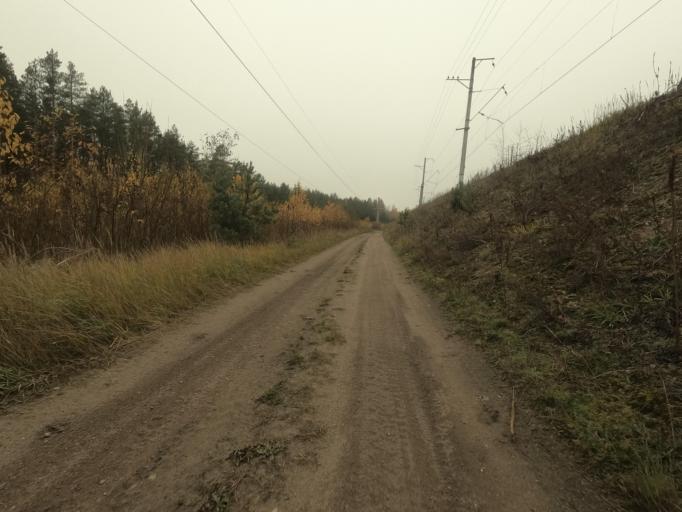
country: RU
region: Leningrad
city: Pavlovo
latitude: 59.7689
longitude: 30.9192
